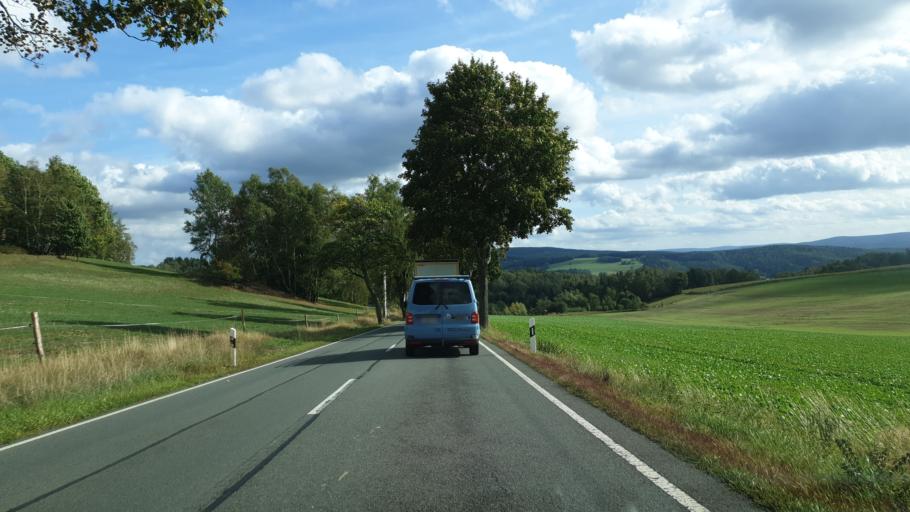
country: DE
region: Saxony
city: Lossnitz
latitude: 50.6434
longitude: 12.7308
